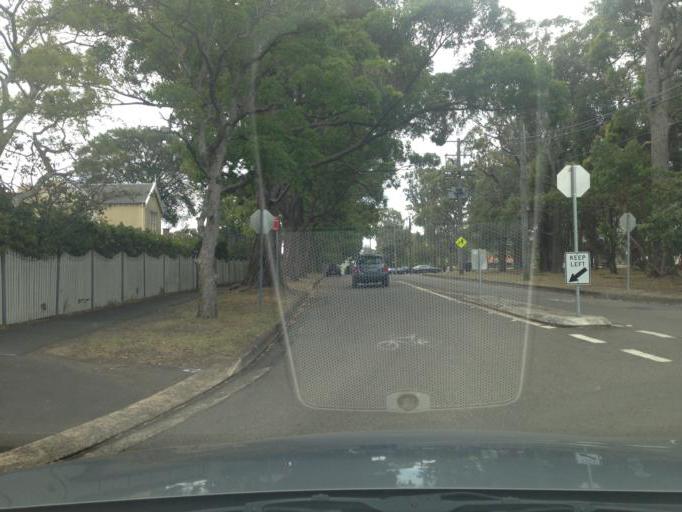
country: AU
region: New South Wales
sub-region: Ku-ring-gai
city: Killara
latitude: -33.7620
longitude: 151.1708
